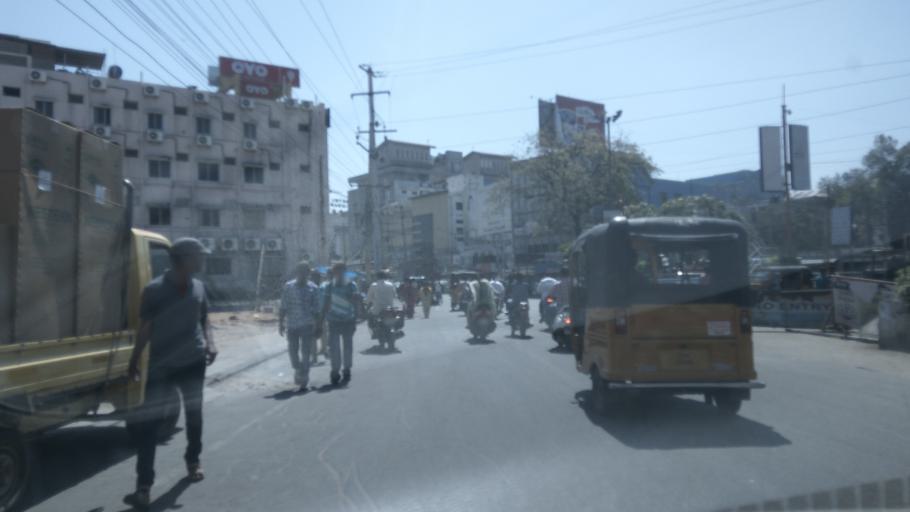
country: IN
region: Andhra Pradesh
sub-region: Chittoor
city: Tirupati
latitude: 13.6294
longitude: 79.4243
